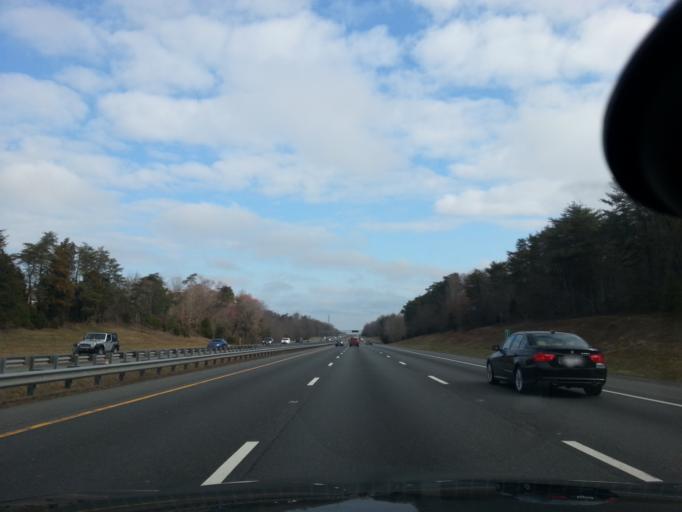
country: US
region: Virginia
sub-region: Spotsylvania County
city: Spotsylvania Courthouse
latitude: 38.1798
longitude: -77.5017
